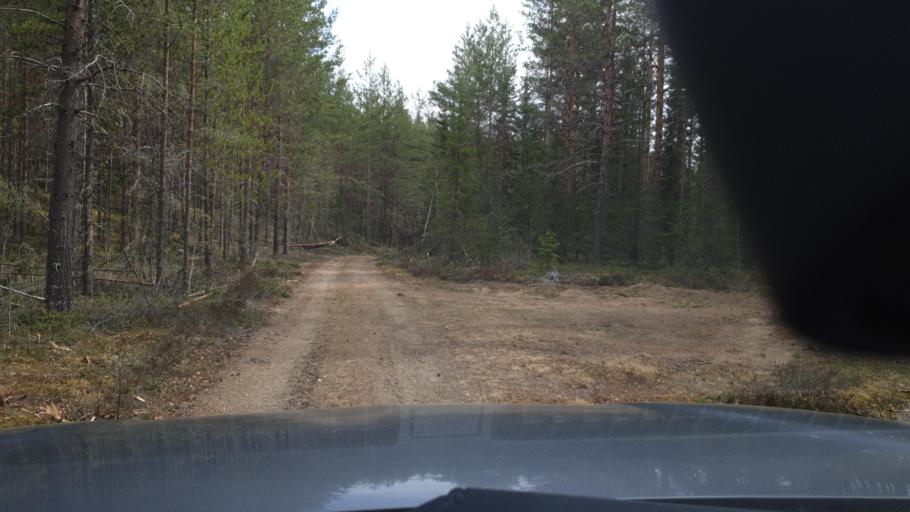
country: SE
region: Vaesternorrland
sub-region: Ange Kommun
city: Ange
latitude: 62.1871
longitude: 15.6157
